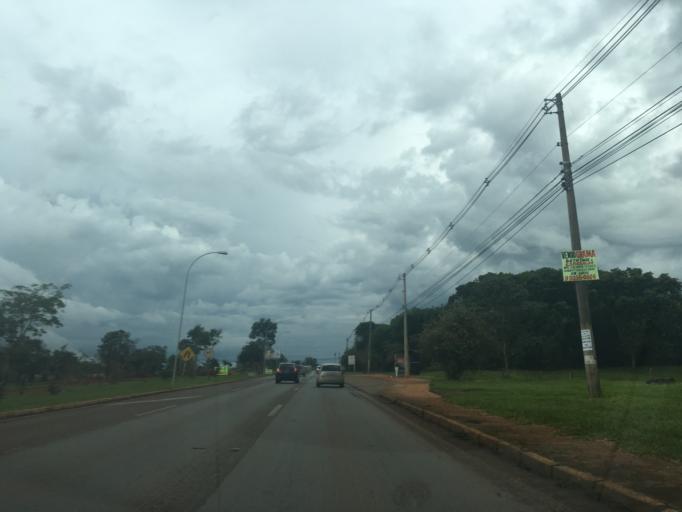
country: BR
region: Federal District
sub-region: Brasilia
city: Brasilia
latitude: -15.7260
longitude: -47.8947
